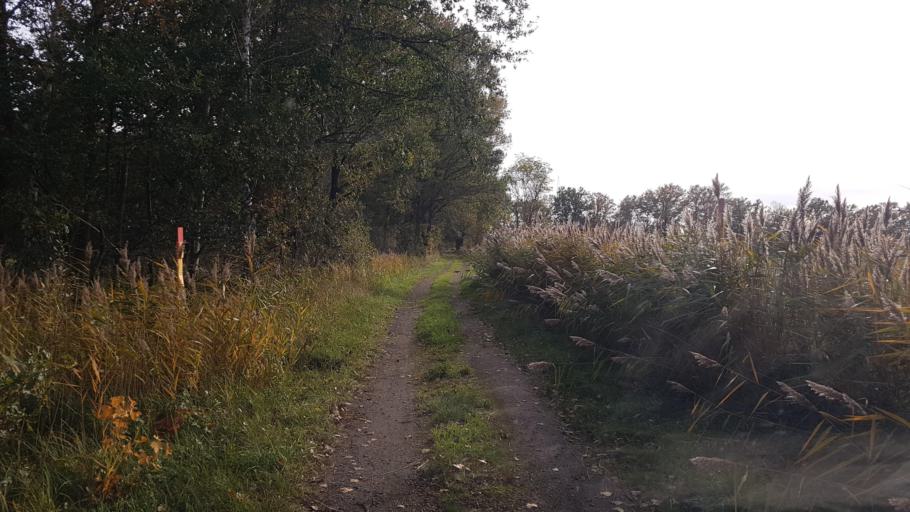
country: DE
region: Brandenburg
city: Schraden
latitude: 51.4543
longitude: 13.6996
